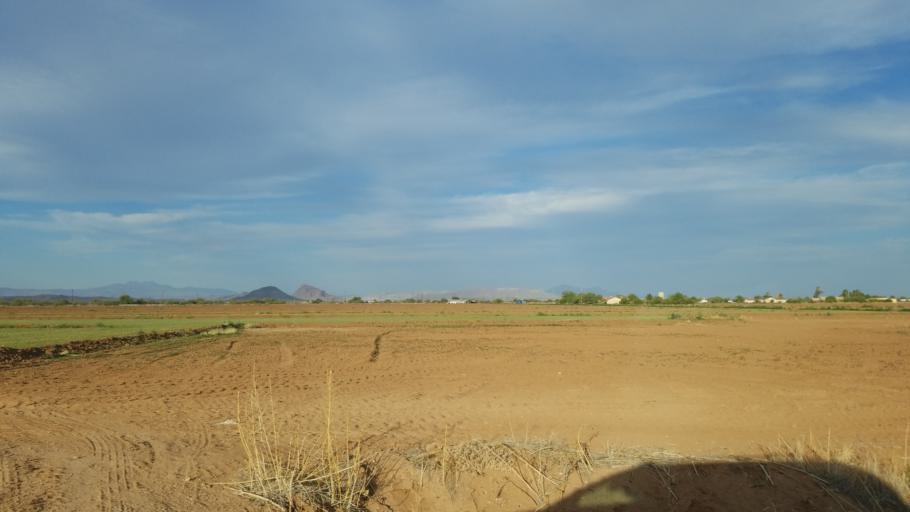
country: US
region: Arizona
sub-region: Maricopa County
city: Scottsdale
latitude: 33.5222
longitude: -111.8654
